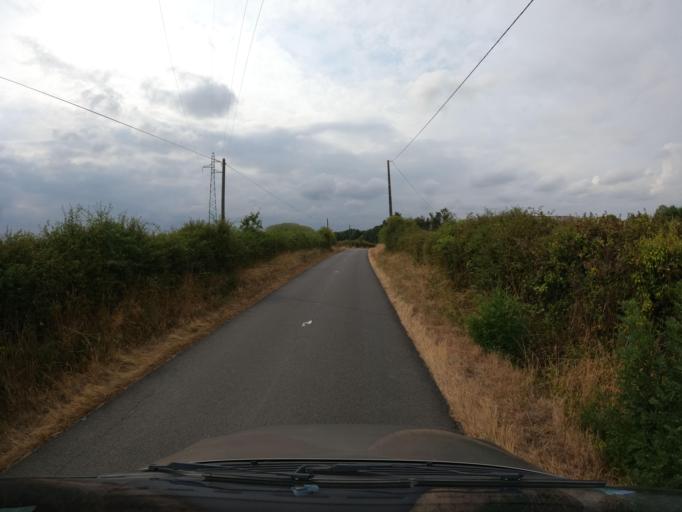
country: FR
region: Pays de la Loire
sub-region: Departement de Maine-et-Loire
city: Saint-Christophe-du-Bois
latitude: 47.0408
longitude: -0.9731
